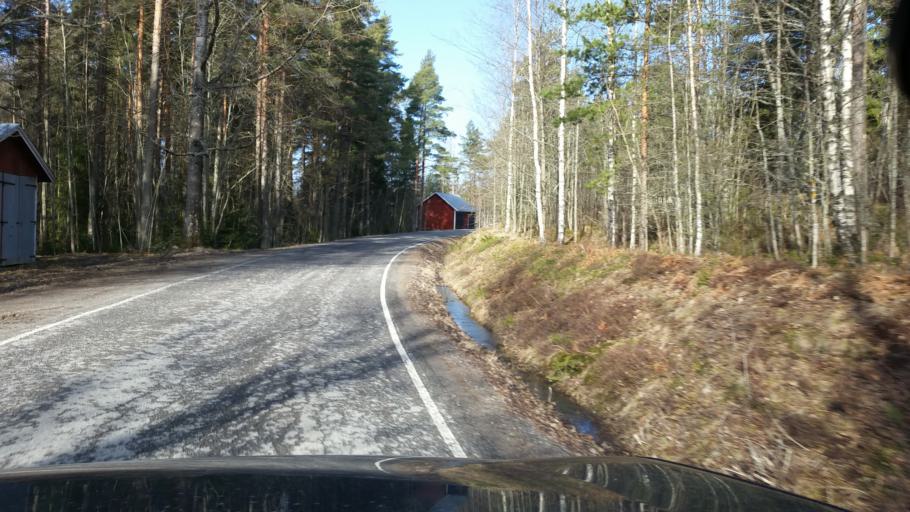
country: FI
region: Uusimaa
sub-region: Raaseporin
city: Inga
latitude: 60.0496
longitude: 24.0362
